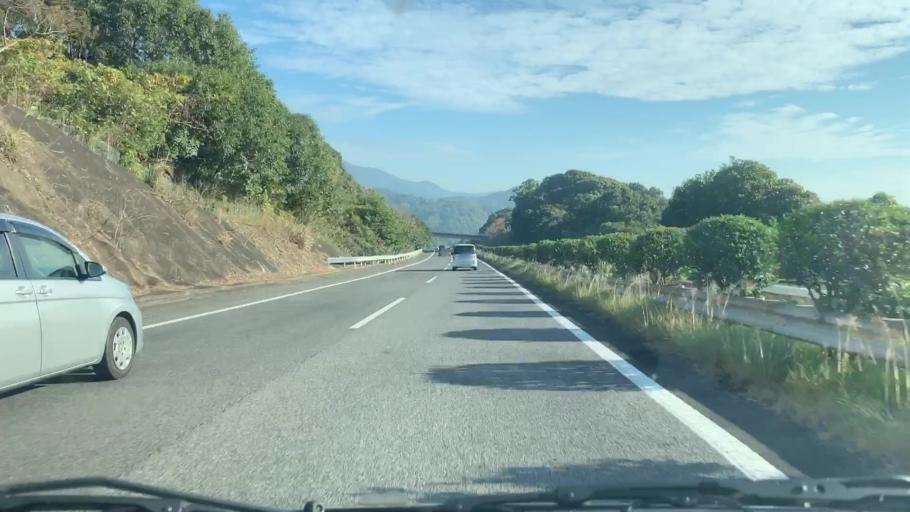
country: JP
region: Saga Prefecture
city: Saga-shi
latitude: 33.2899
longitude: 130.1641
